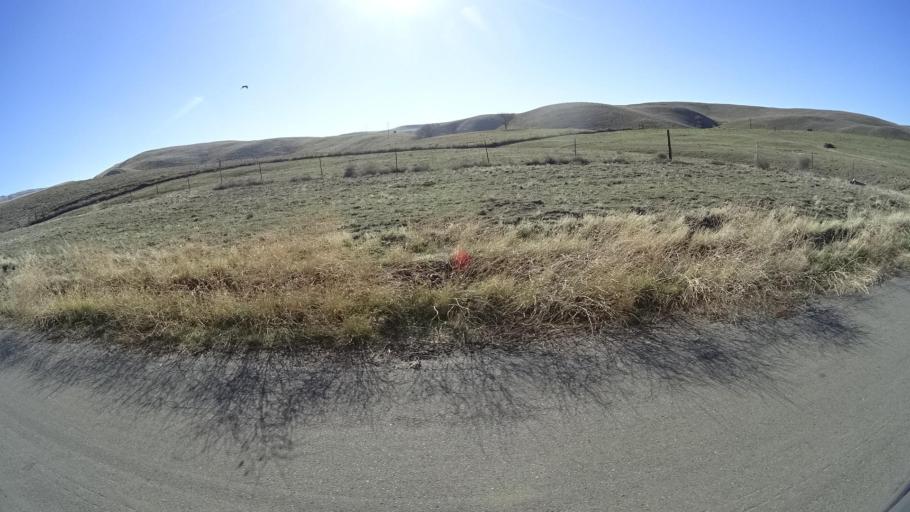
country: US
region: California
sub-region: Kern County
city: Maricopa
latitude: 34.9724
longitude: -119.4569
